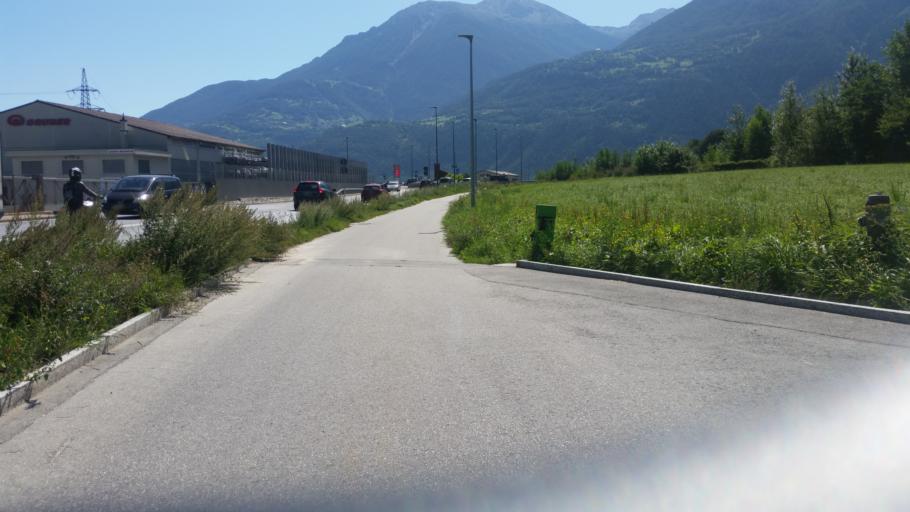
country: CH
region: Valais
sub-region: Leuk District
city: Leuk
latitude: 46.3095
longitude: 7.6495
